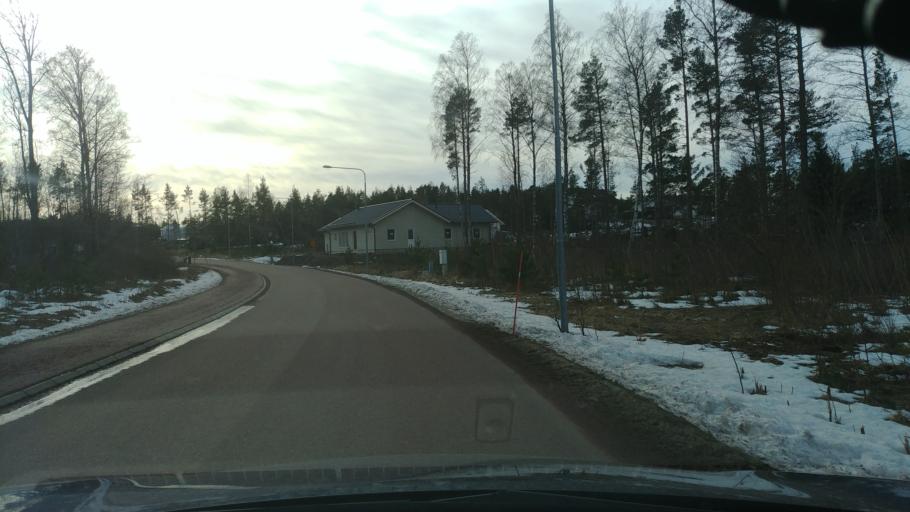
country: AX
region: Mariehamns stad
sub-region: Mariehamn
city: Mariehamn
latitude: 60.1022
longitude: 19.8929
